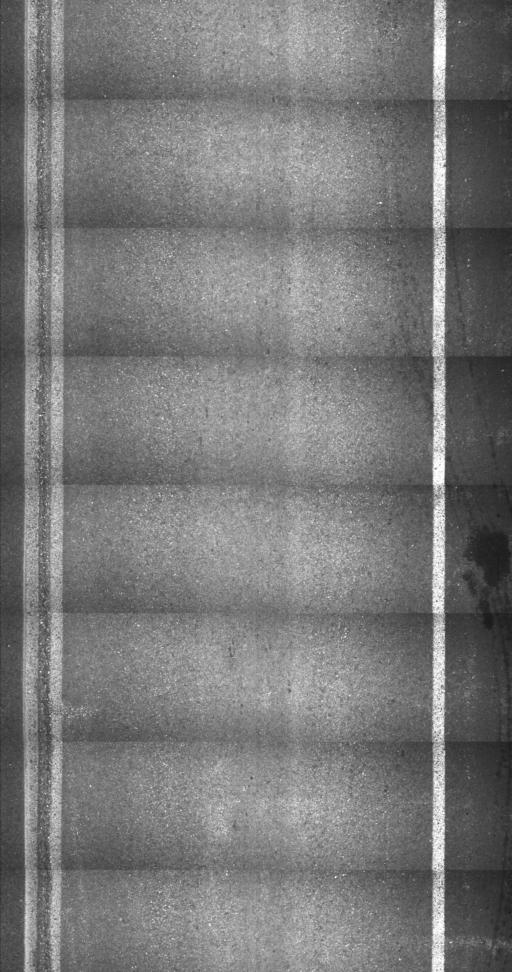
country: CA
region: Quebec
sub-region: Monteregie
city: Sutton
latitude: 44.9848
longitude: -72.5055
